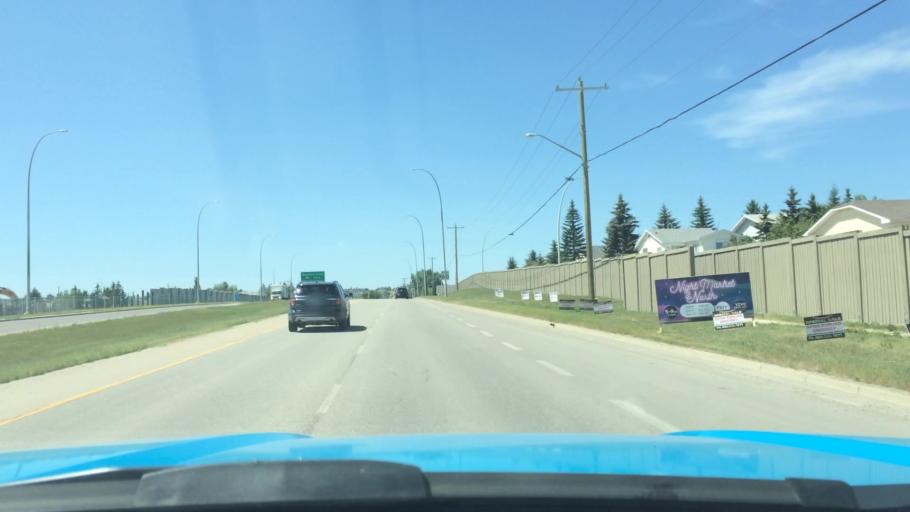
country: CA
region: Alberta
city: Calgary
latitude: 51.1544
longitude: -114.0434
